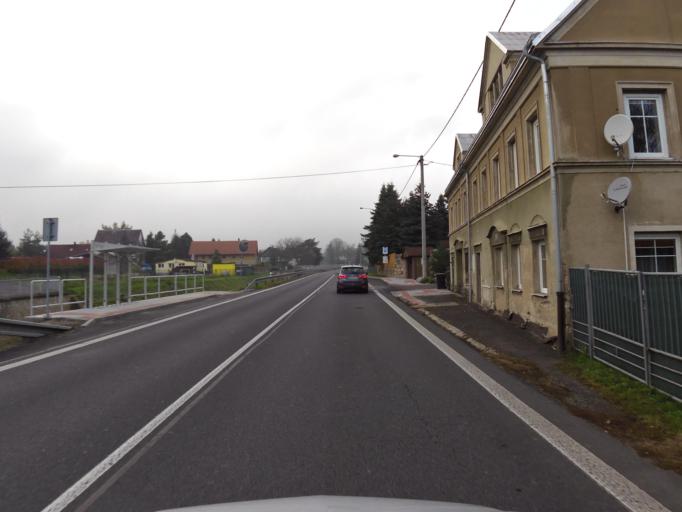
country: CZ
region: Ustecky
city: Libouchec
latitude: 50.7587
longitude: 14.0686
